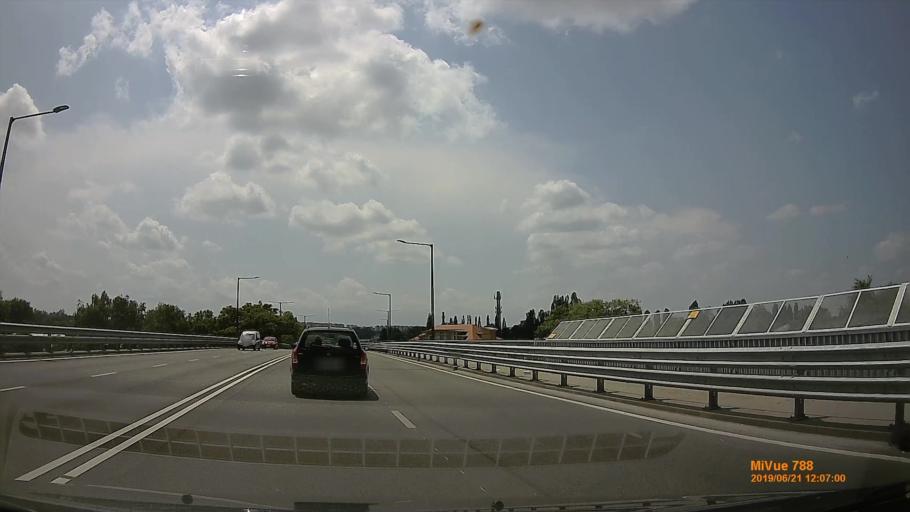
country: HU
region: Baranya
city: Pecs
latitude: 46.0685
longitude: 18.2330
